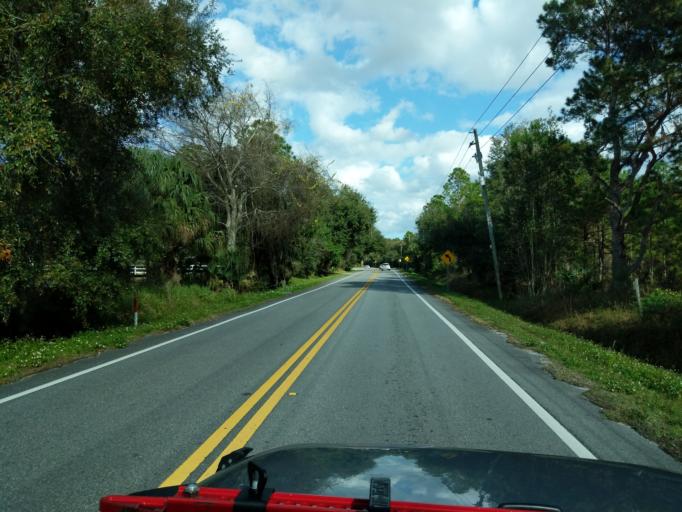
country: US
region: Florida
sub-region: Seminole County
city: Geneva
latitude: 28.6956
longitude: -81.1410
